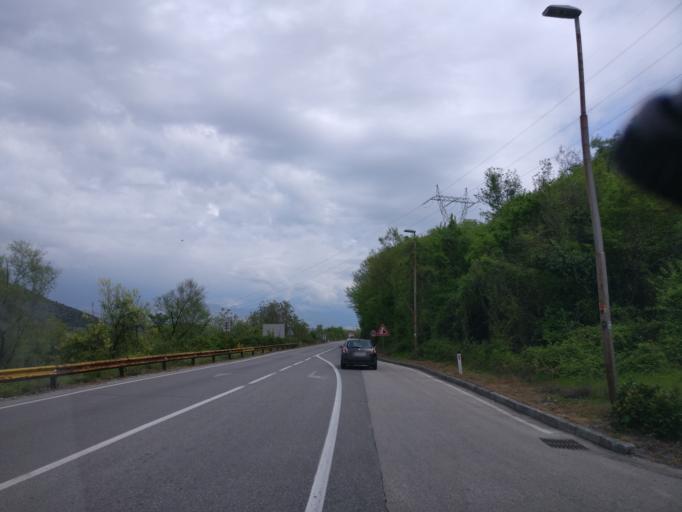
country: ME
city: Spuz
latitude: 42.4554
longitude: 19.1875
